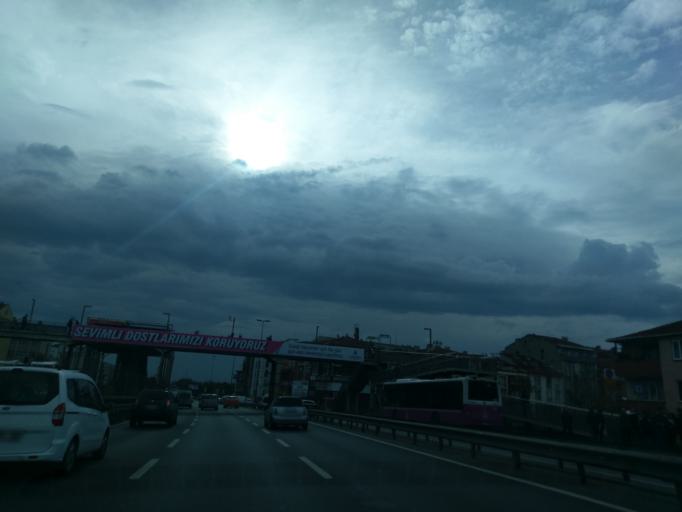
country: TR
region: Istanbul
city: Bahcelievler
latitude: 40.9955
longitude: 28.7952
